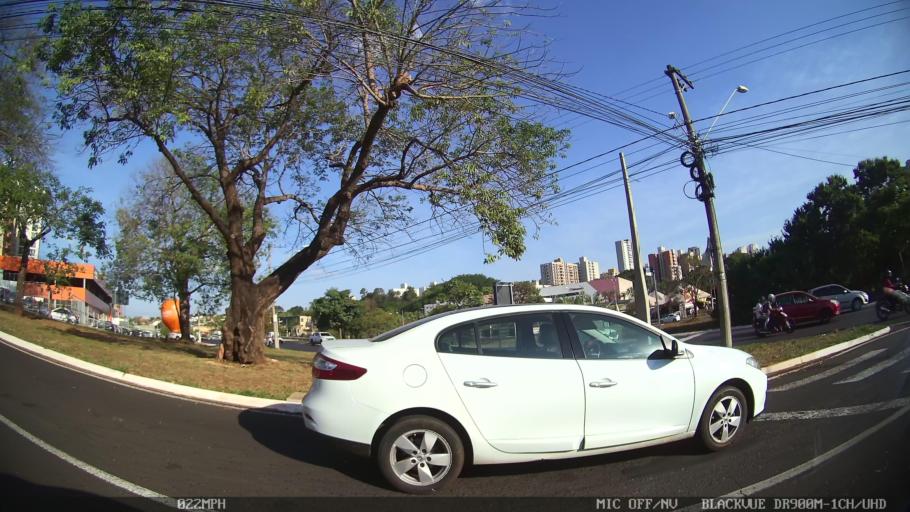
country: BR
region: Sao Paulo
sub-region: Ribeirao Preto
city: Ribeirao Preto
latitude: -21.2071
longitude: -47.7902
